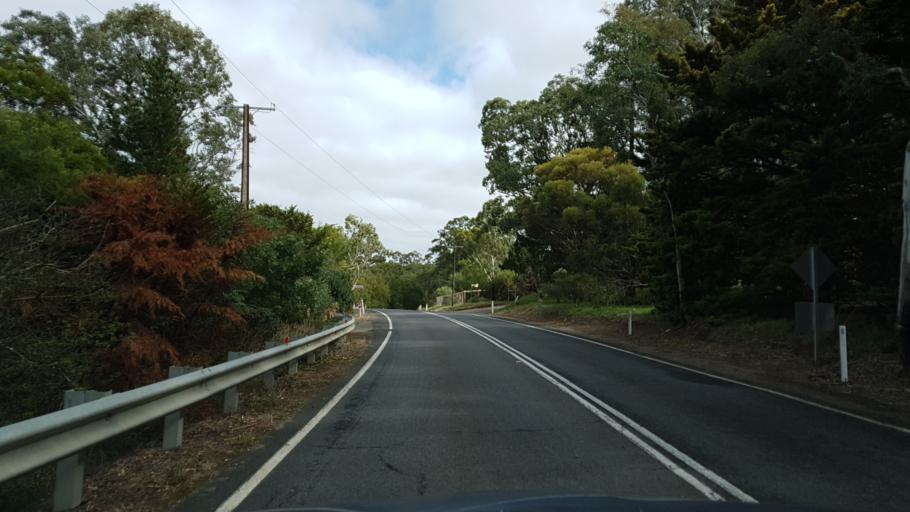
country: AU
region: South Australia
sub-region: Mount Barker
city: Nairne
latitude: -35.0412
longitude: 138.9266
